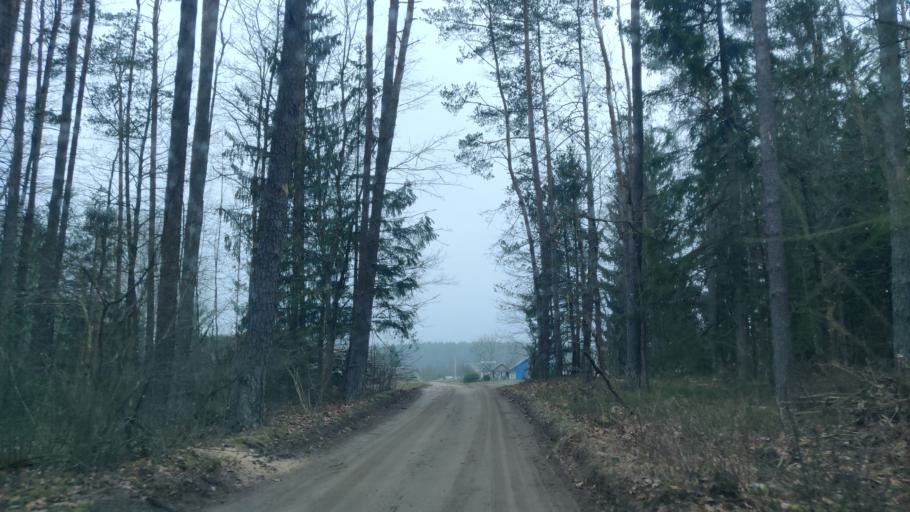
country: LT
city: Trakai
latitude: 54.5588
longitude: 24.9343
